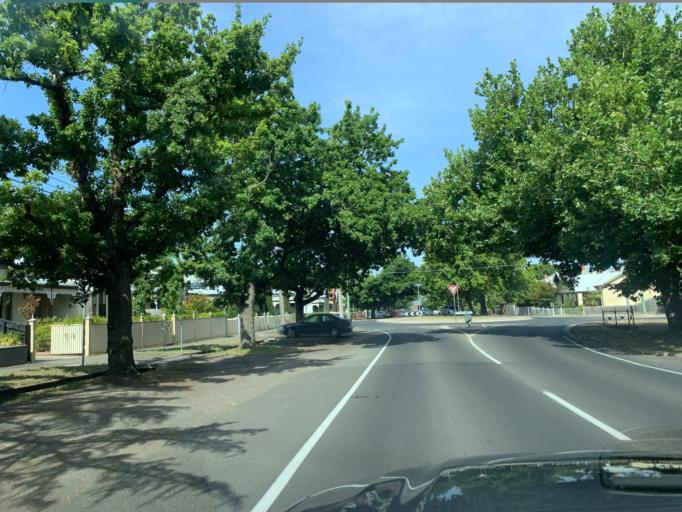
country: AU
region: Victoria
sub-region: Ballarat North
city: Lake Wendouree
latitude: -37.5578
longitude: 143.8412
